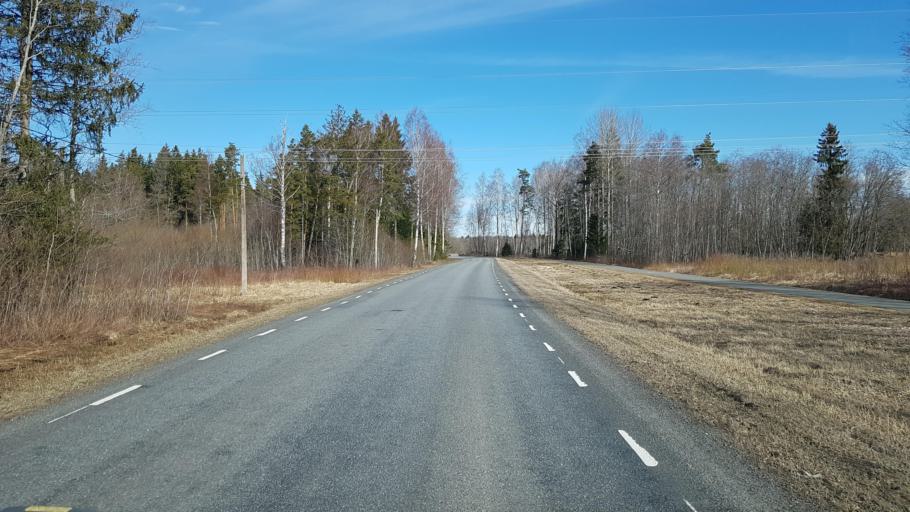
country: EE
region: Harju
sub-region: Nissi vald
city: Riisipere
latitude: 59.2341
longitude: 24.2445
